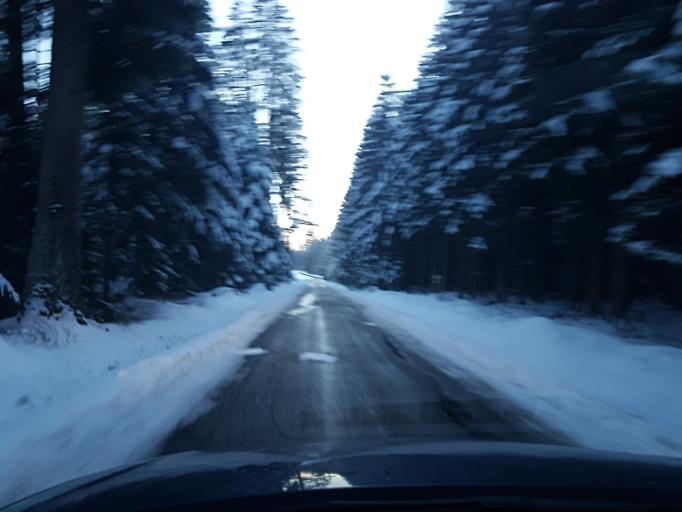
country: DE
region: Baden-Wuerttemberg
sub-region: Freiburg Region
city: Unterkirnach
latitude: 48.0916
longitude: 8.3684
